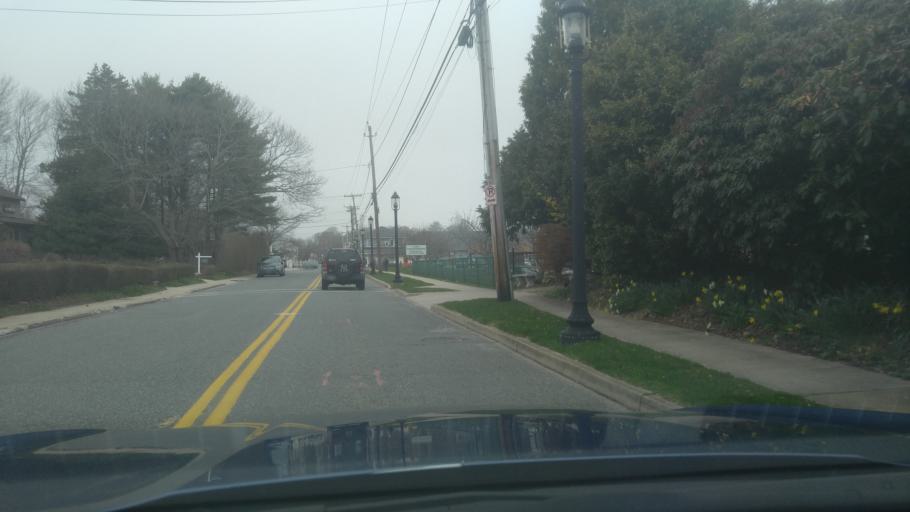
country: US
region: Rhode Island
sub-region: Washington County
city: Narragansett Pier
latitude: 41.4246
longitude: -71.4604
